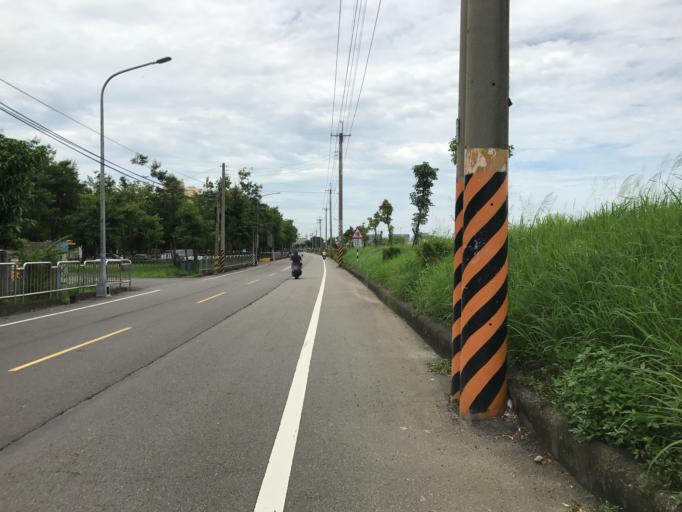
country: TW
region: Taiwan
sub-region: Taichung City
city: Taichung
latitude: 24.0803
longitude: 120.7127
